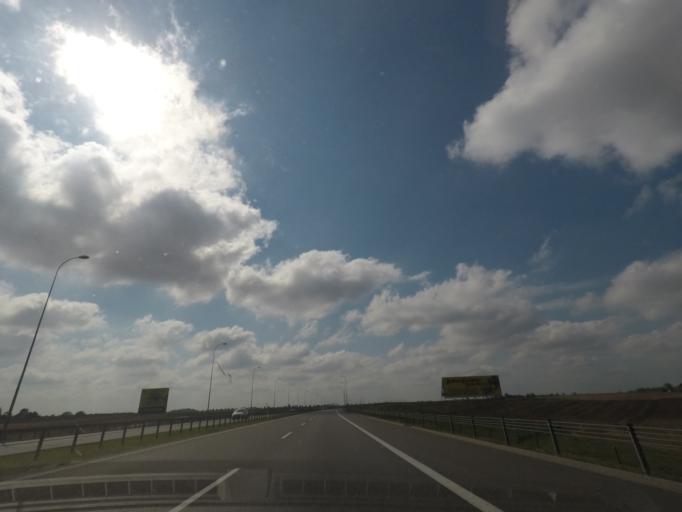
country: PL
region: Kujawsko-Pomorskie
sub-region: Powiat chelminski
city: Lisewo
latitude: 53.2649
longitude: 18.7217
